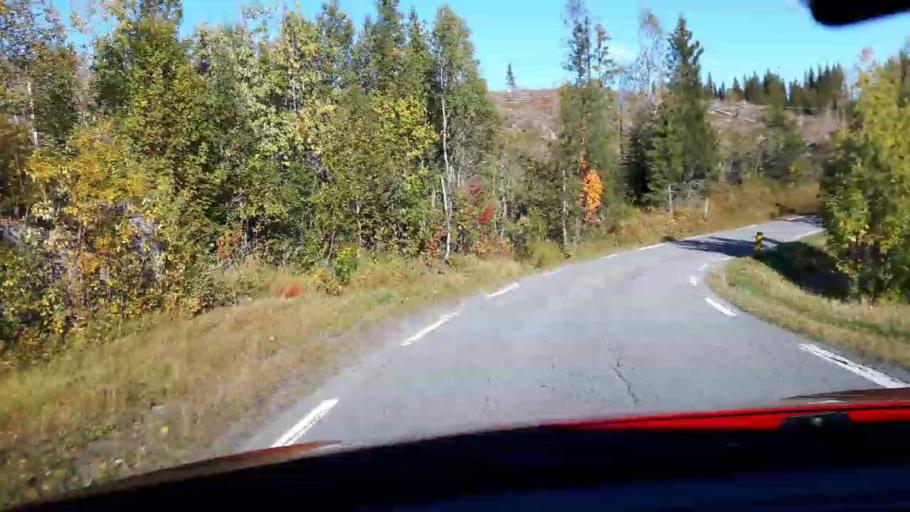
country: NO
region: Nord-Trondelag
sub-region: Lierne
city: Sandvika
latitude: 64.6359
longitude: 13.6967
